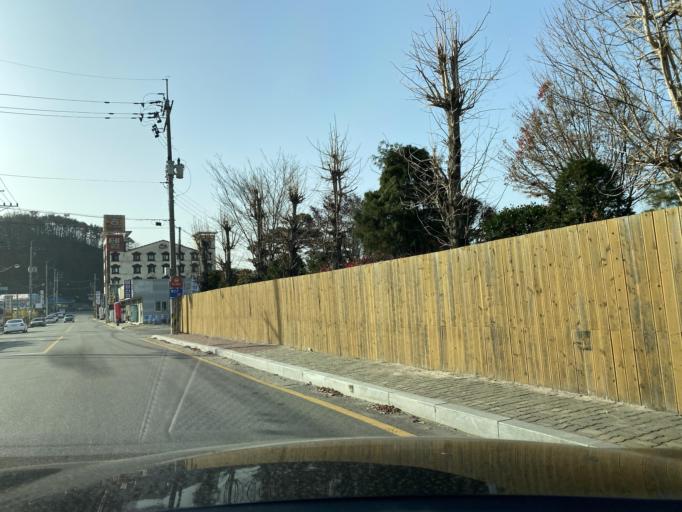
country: KR
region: Chungcheongnam-do
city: Yesan
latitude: 36.6813
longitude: 126.8290
